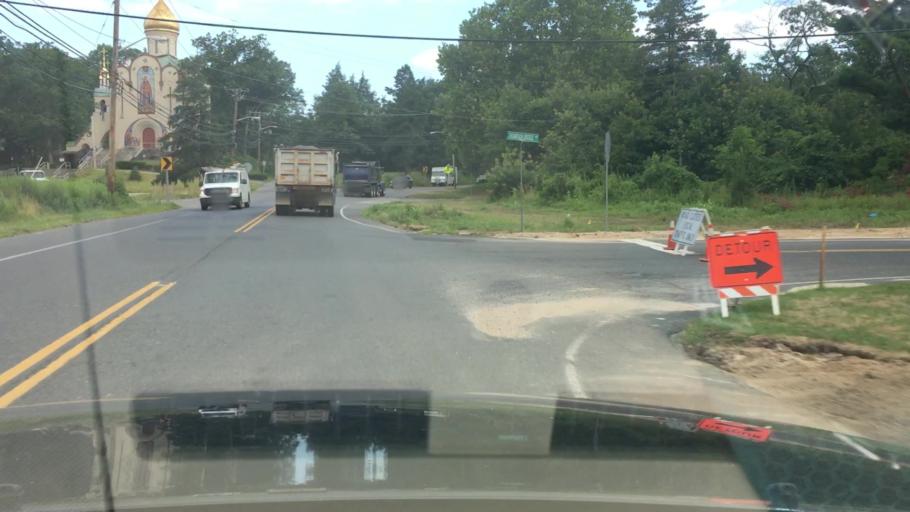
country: US
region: New Jersey
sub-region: Ocean County
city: Vista Center
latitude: 40.1112
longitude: -74.3891
